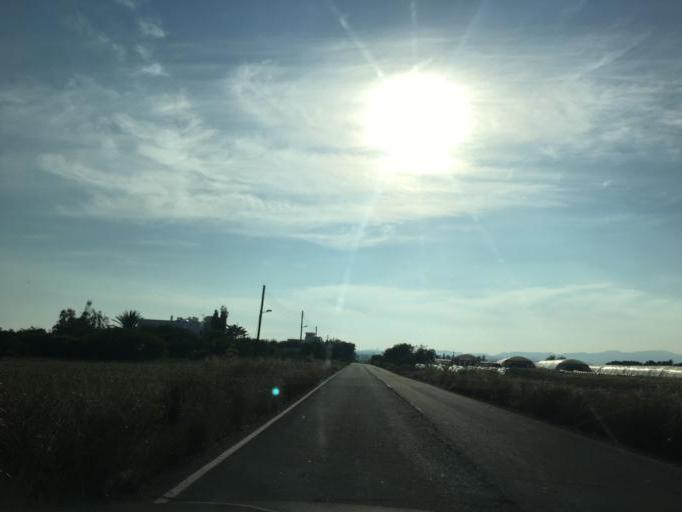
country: CY
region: Larnaka
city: Kofinou
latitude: 34.7330
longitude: 33.3591
